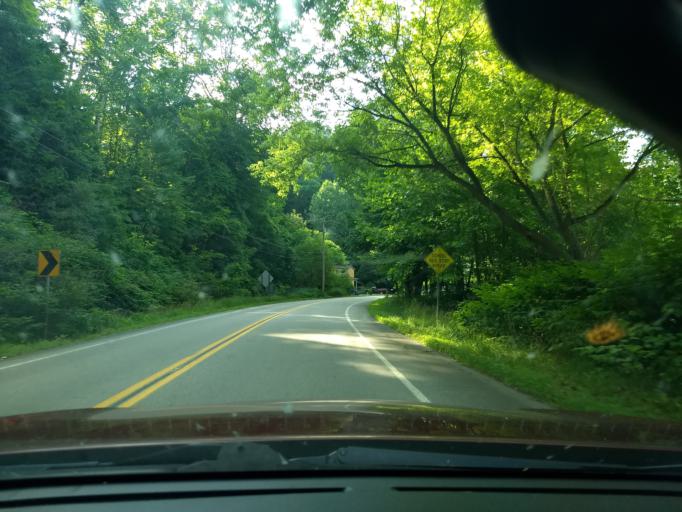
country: US
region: Pennsylvania
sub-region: Westmoreland County
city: Irwin
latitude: 40.3391
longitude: -79.7244
